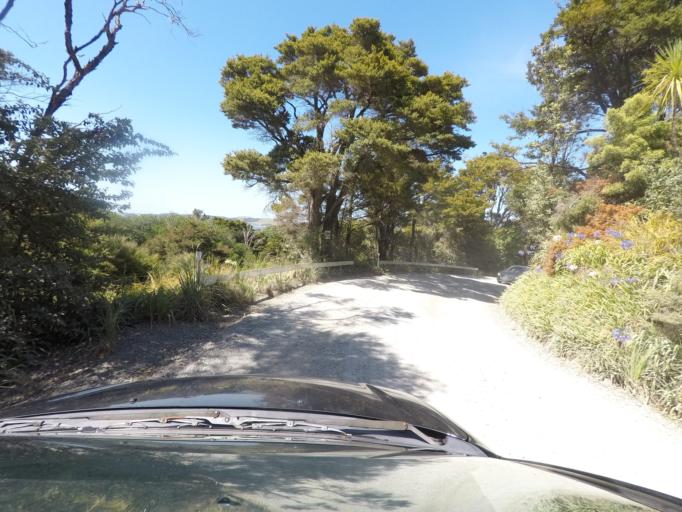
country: NZ
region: Auckland
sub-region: Auckland
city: Warkworth
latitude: -36.3168
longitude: 174.7912
